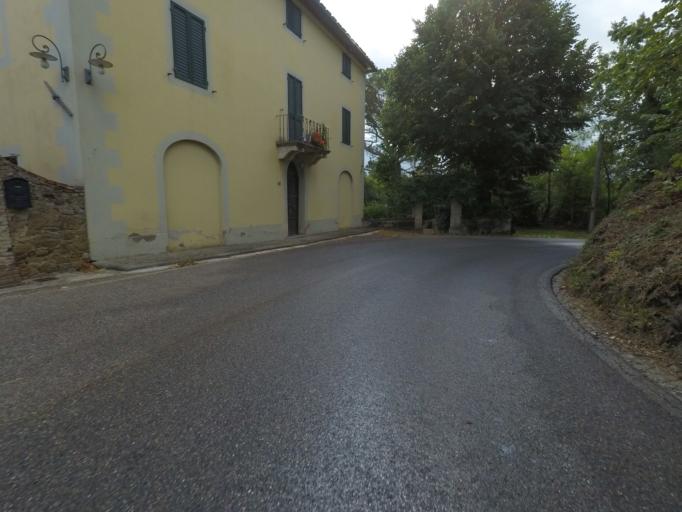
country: IT
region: Tuscany
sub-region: Provincia di Siena
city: Radda in Chianti
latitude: 43.4146
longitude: 11.3504
